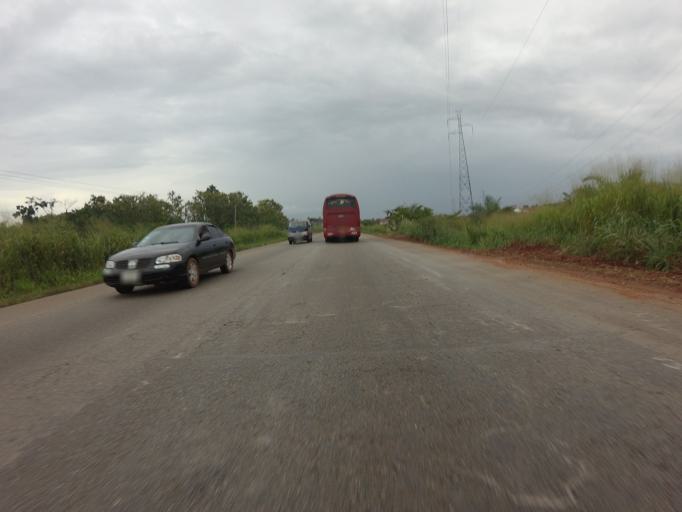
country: GH
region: Ashanti
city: Konongo
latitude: 6.6167
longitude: -1.1729
